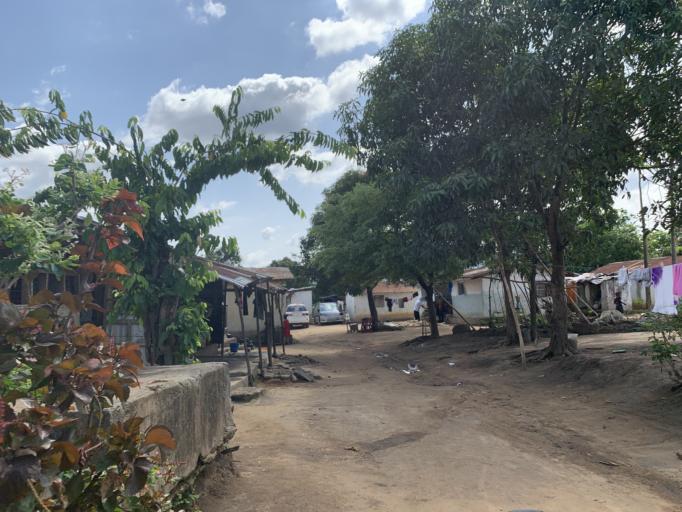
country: SL
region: Western Area
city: Waterloo
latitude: 8.3335
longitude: -13.0496
